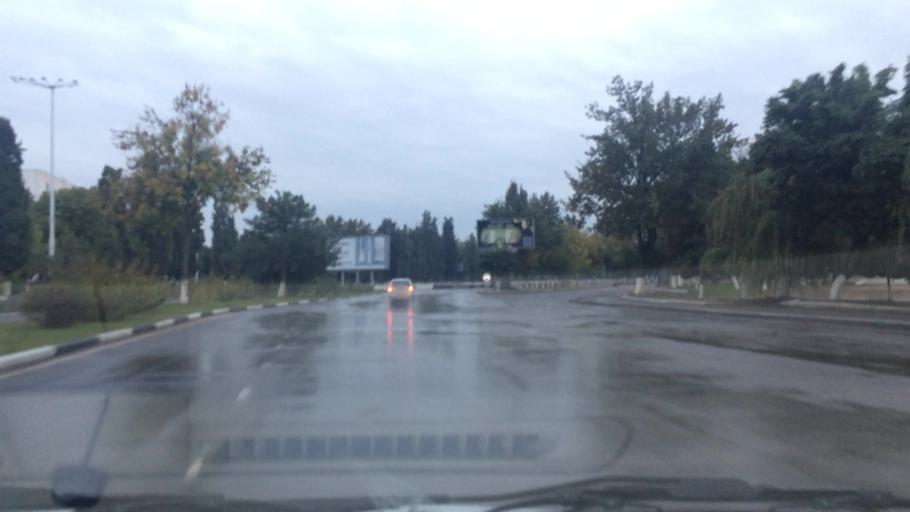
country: UZ
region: Toshkent Shahri
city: Tashkent
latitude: 41.3114
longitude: 69.2403
